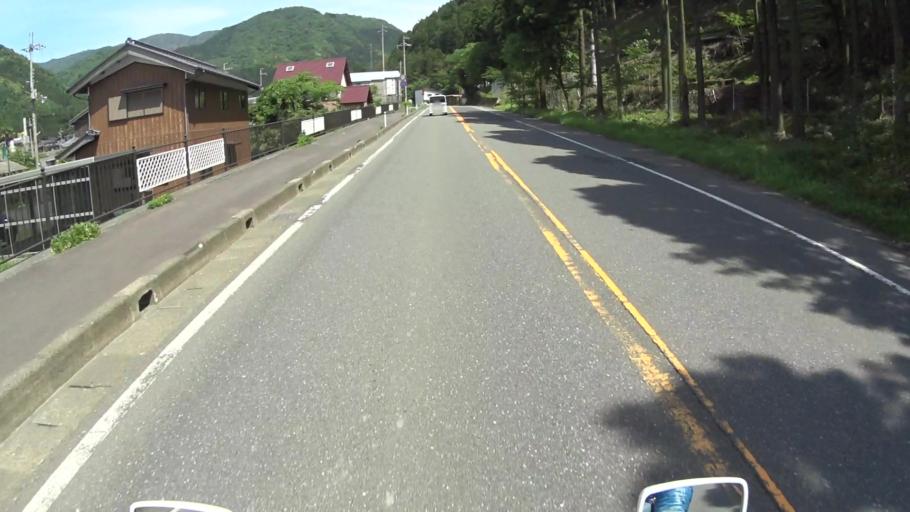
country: JP
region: Fukui
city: Obama
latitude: 35.4492
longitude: 135.8910
